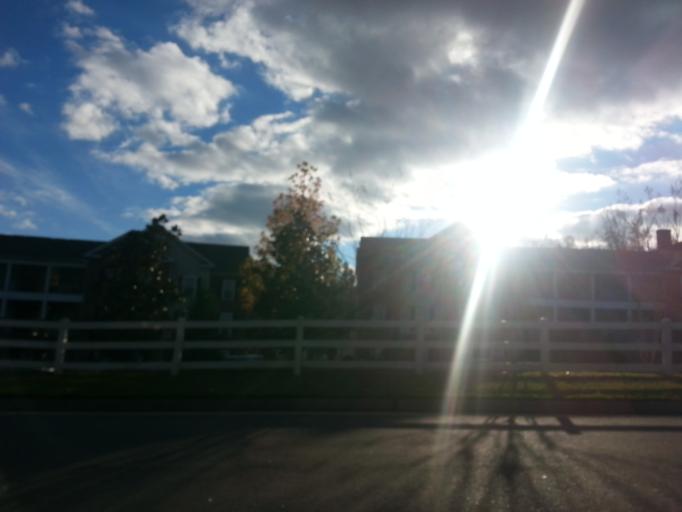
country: US
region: Tennessee
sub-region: Knox County
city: Knoxville
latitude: 35.9344
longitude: -83.9317
